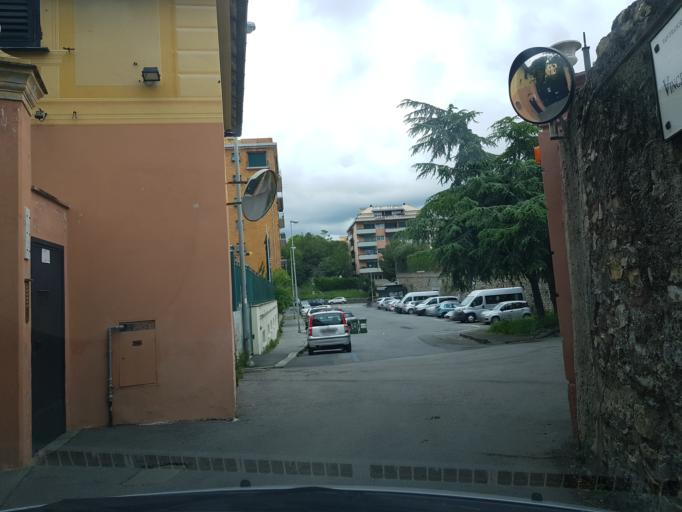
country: IT
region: Liguria
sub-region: Provincia di Genova
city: San Teodoro
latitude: 44.3965
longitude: 8.9653
